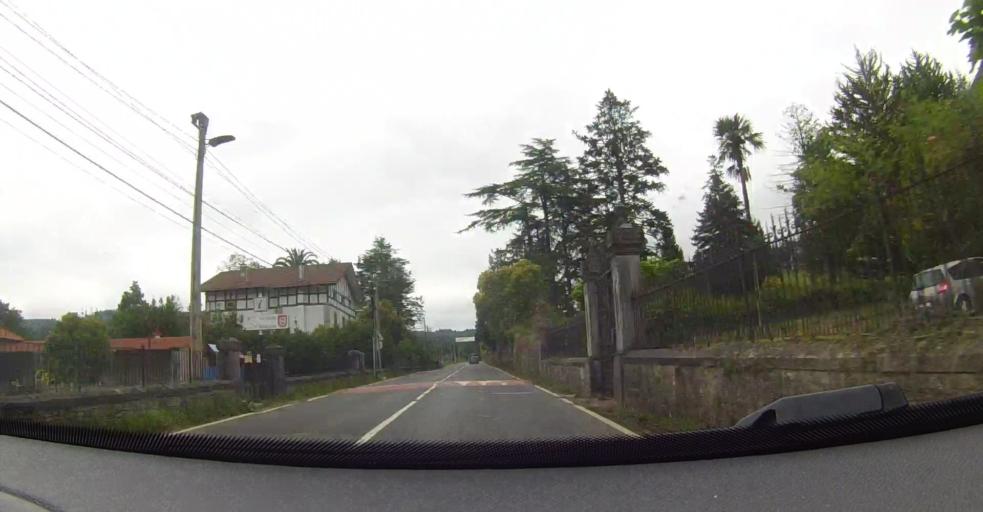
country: ES
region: Basque Country
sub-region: Bizkaia
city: Balmaseda
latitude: 43.2442
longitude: -3.2607
